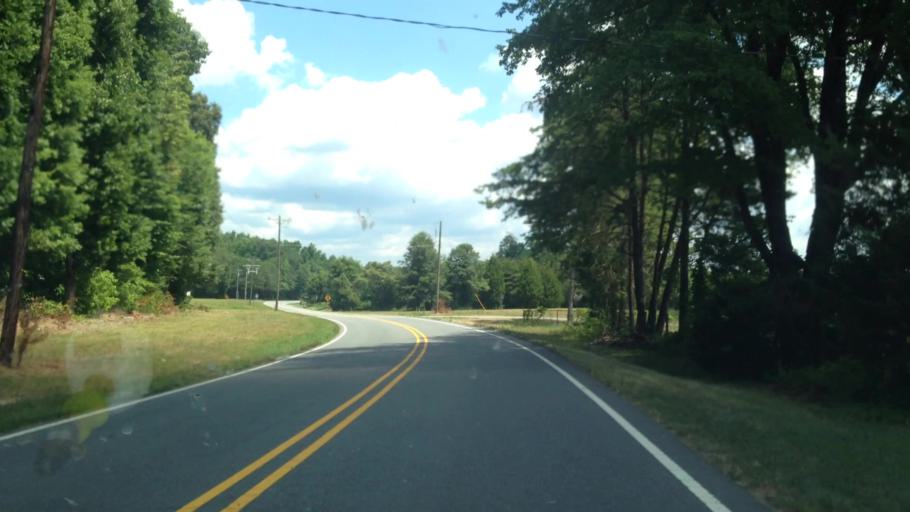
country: US
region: North Carolina
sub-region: Guilford County
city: Oak Ridge
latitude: 36.2048
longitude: -80.0033
